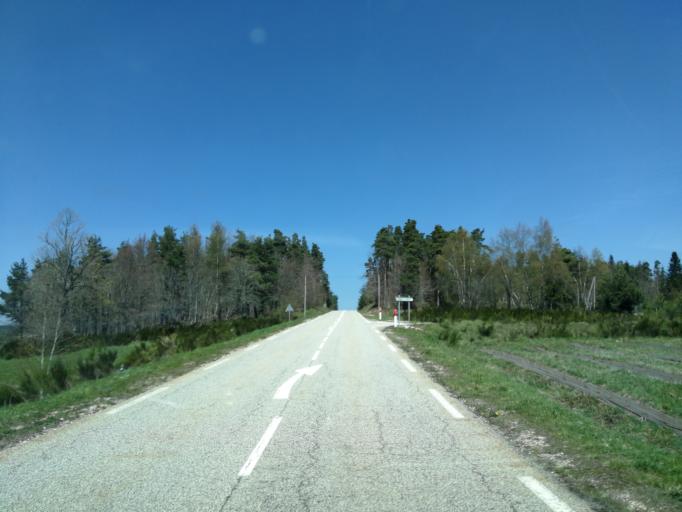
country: FR
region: Rhone-Alpes
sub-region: Departement de l'Ardeche
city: Saint-Agreve
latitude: 45.0484
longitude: 4.4048
